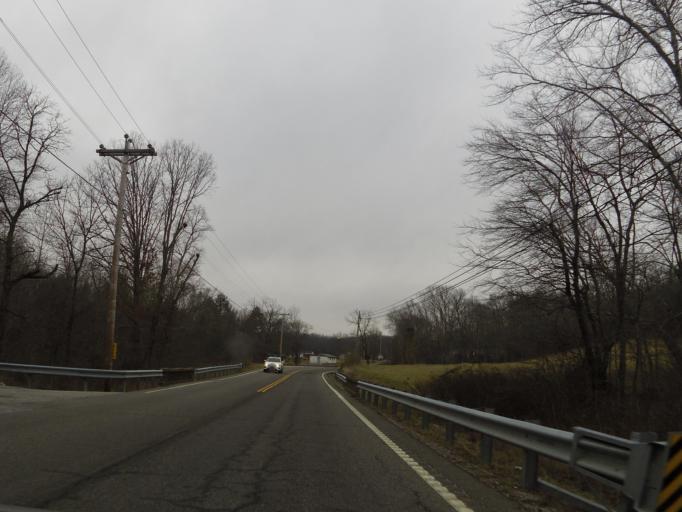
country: US
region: Tennessee
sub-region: Morgan County
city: Wartburg
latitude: 36.1791
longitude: -84.6585
